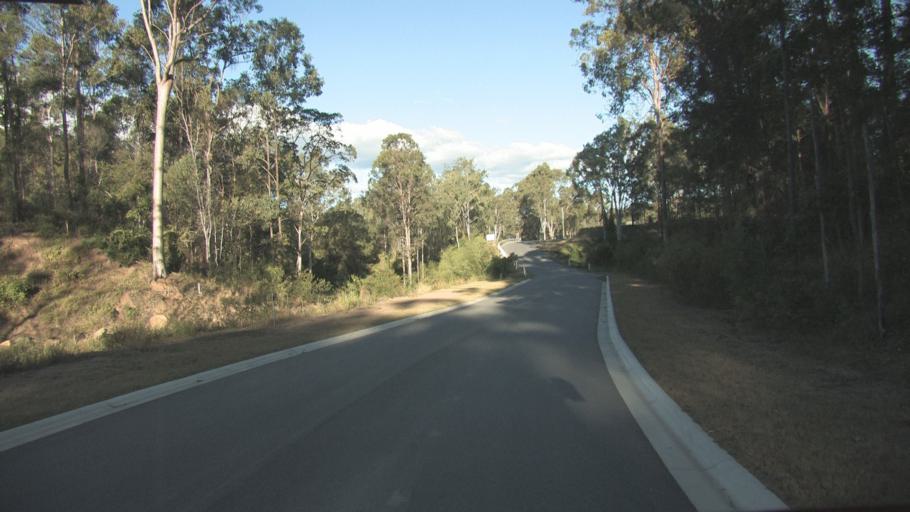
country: AU
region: Queensland
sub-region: Logan
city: Cedar Vale
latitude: -27.9281
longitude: 153.0511
